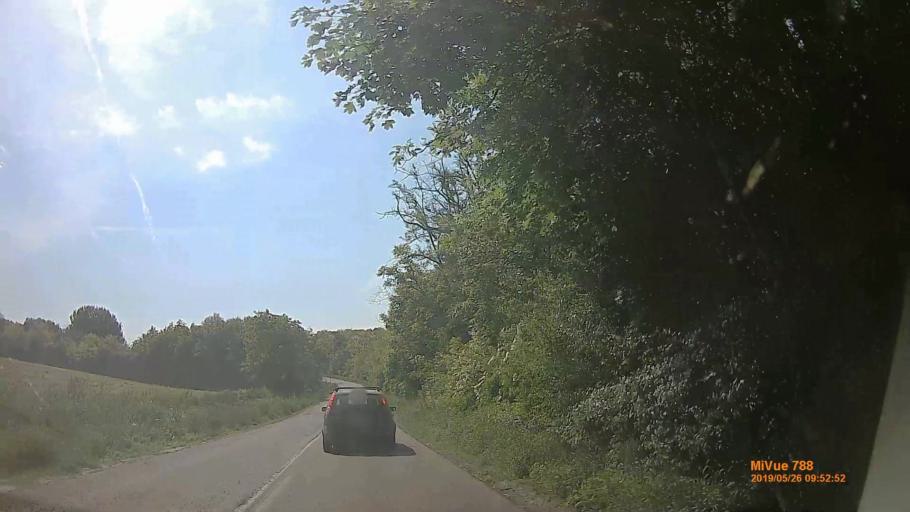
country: HU
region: Fejer
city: Lepseny
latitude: 46.9824
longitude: 18.1956
